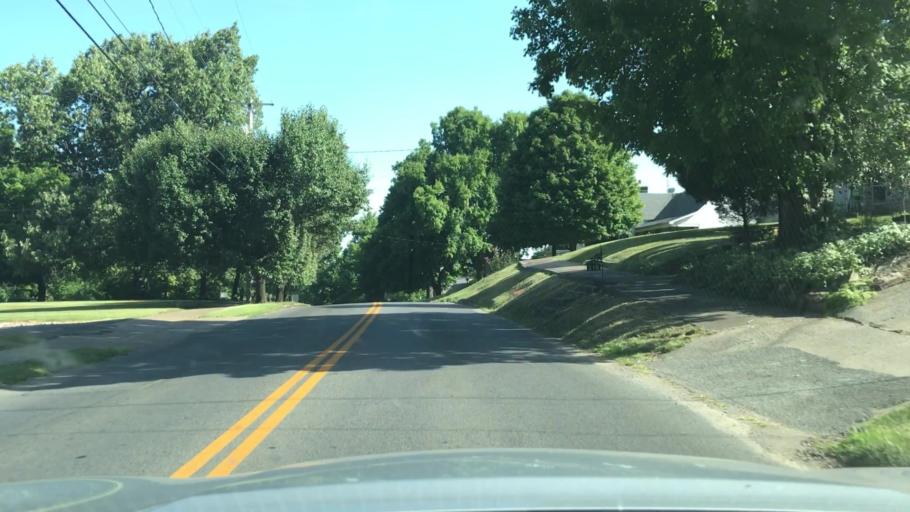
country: US
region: Kentucky
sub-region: Muhlenberg County
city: Greenville
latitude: 37.2060
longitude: -87.1791
